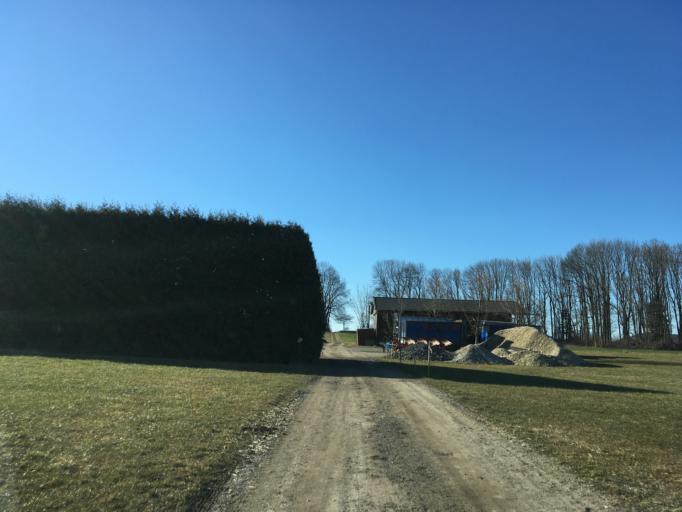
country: DE
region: Bavaria
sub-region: Upper Bavaria
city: Bruckmuhl
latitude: 47.8643
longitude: 11.9154
